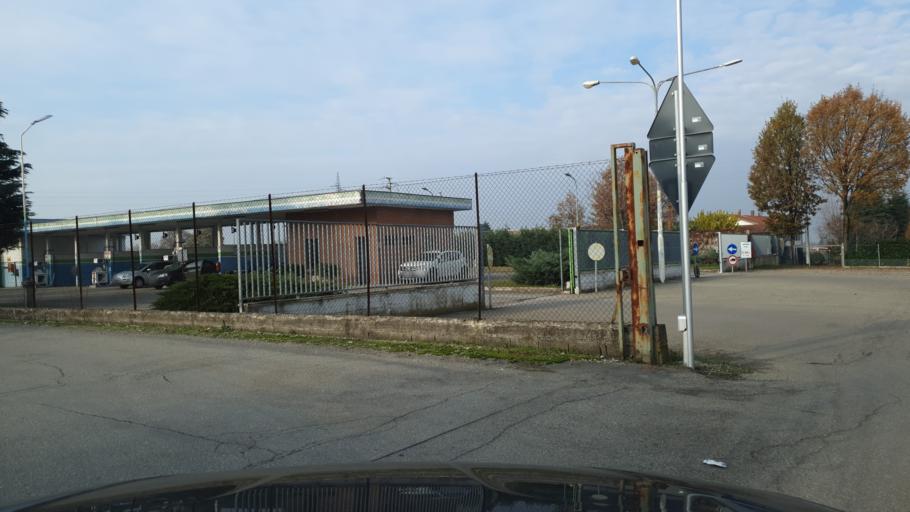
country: IT
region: Emilia-Romagna
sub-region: Provincia di Bologna
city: Bazzano
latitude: 44.5080
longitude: 11.1047
